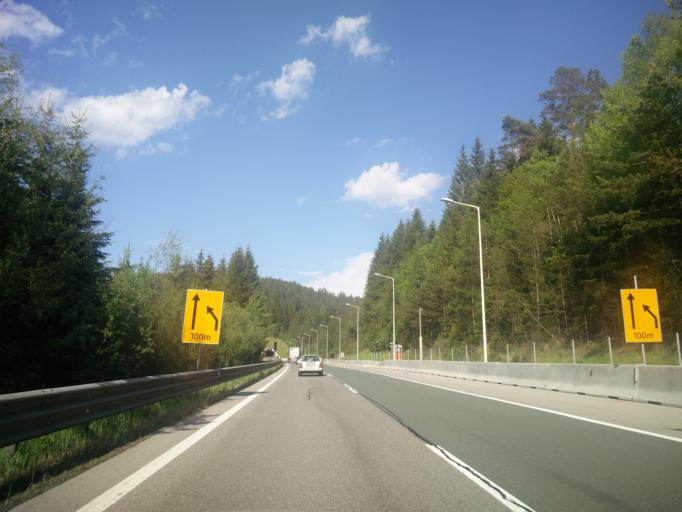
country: AT
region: Styria
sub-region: Politischer Bezirk Voitsberg
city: Modriach
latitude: 46.9624
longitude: 15.0575
